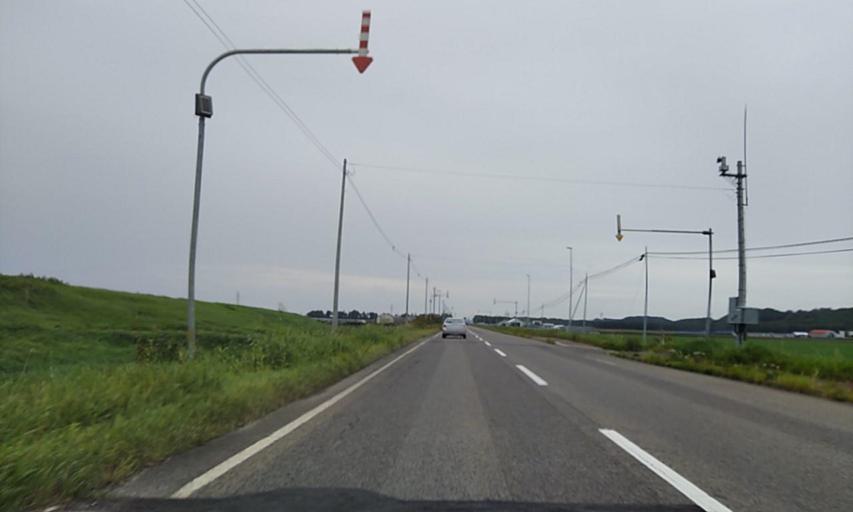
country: JP
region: Hokkaido
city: Bihoro
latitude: 43.8506
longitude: 144.1189
